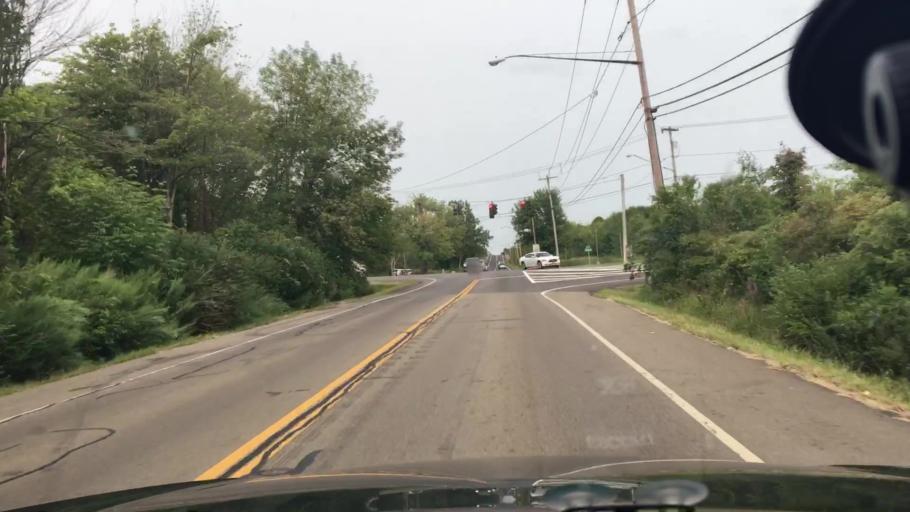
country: US
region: New York
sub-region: Erie County
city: Wanakah
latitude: 42.7075
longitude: -78.9206
